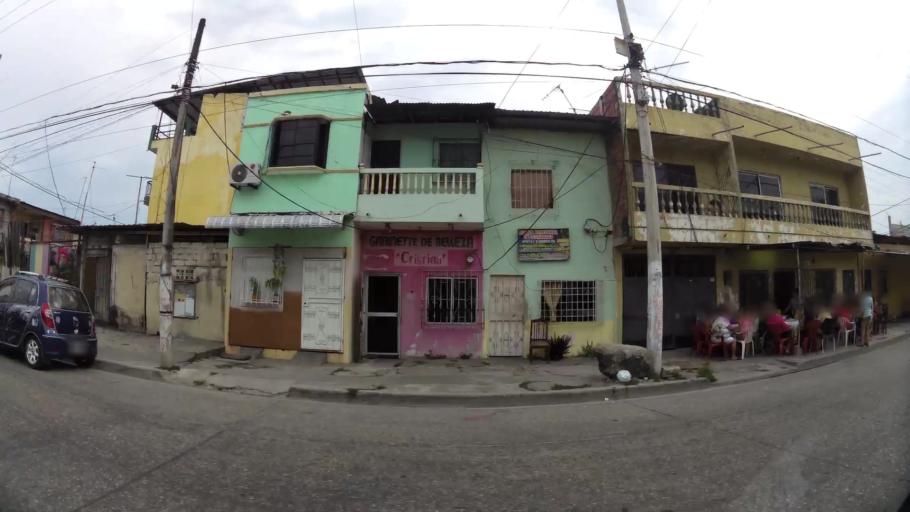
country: EC
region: Guayas
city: Guayaquil
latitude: -2.2462
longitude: -79.8818
